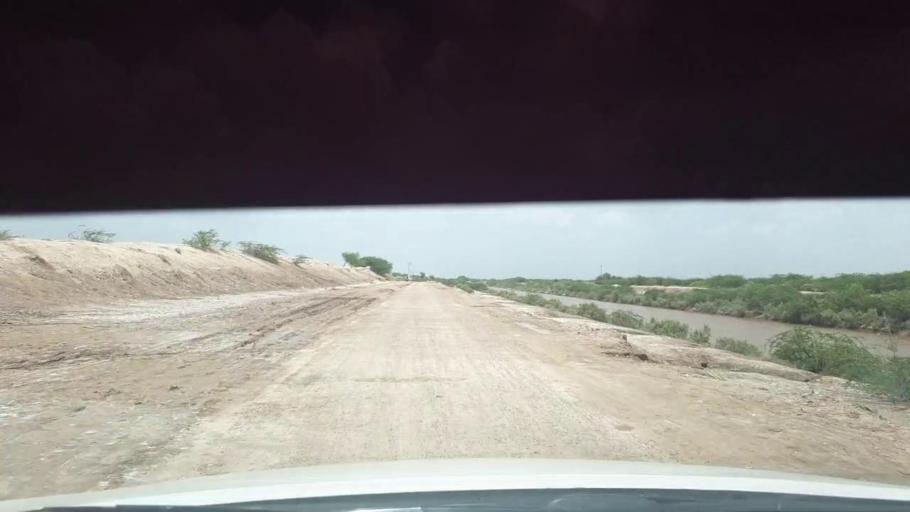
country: PK
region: Sindh
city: Kadhan
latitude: 24.5178
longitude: 69.1210
